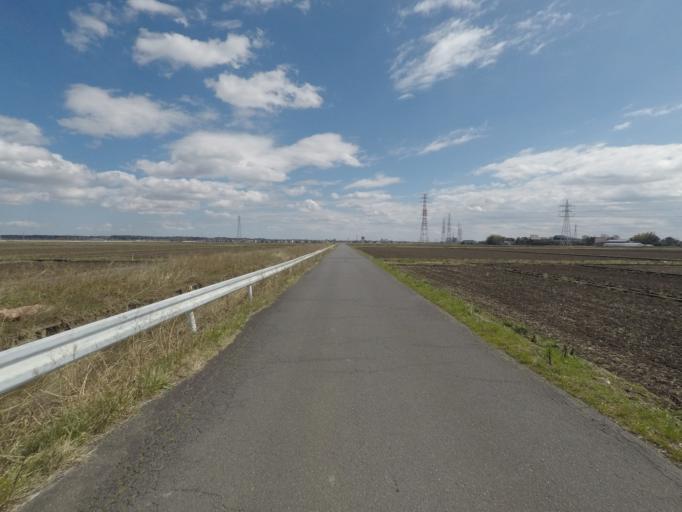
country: JP
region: Ibaraki
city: Fujishiro
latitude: 35.9407
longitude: 140.1076
